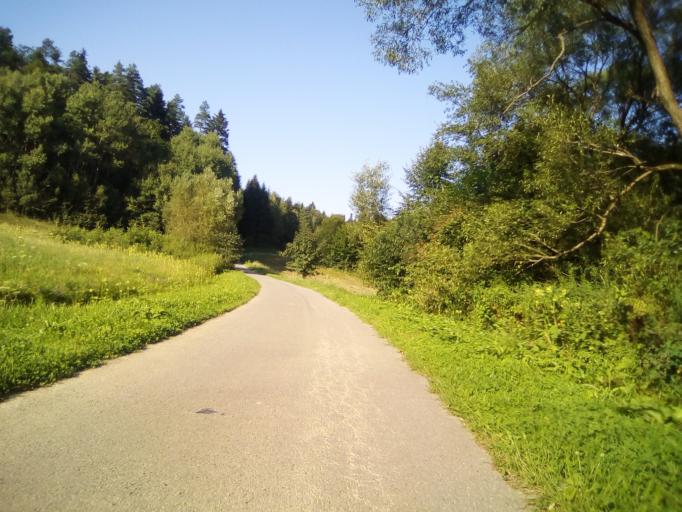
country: PL
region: Subcarpathian Voivodeship
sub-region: Powiat brzozowski
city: Domaradz
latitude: 49.8137
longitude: 21.9459
